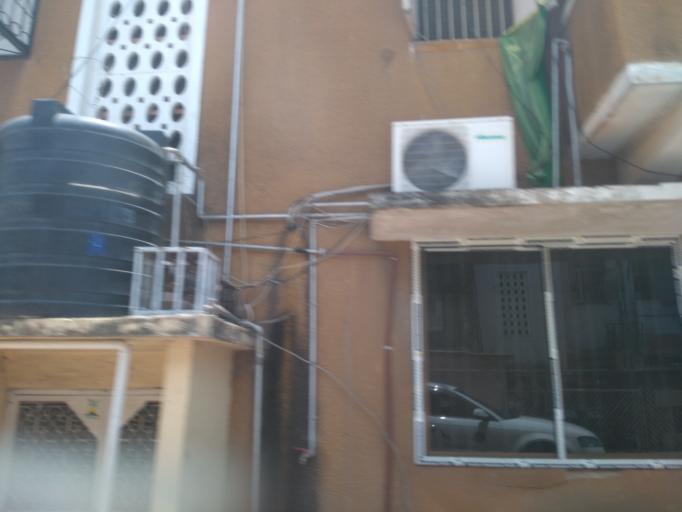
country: TZ
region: Dar es Salaam
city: Dar es Salaam
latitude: -6.8125
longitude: 39.2745
